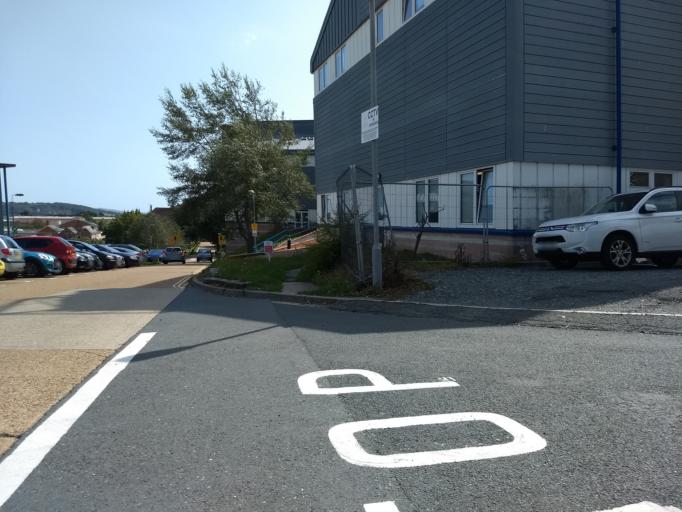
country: GB
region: England
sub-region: Isle of Wight
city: Newport
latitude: 50.7117
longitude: -1.3001
